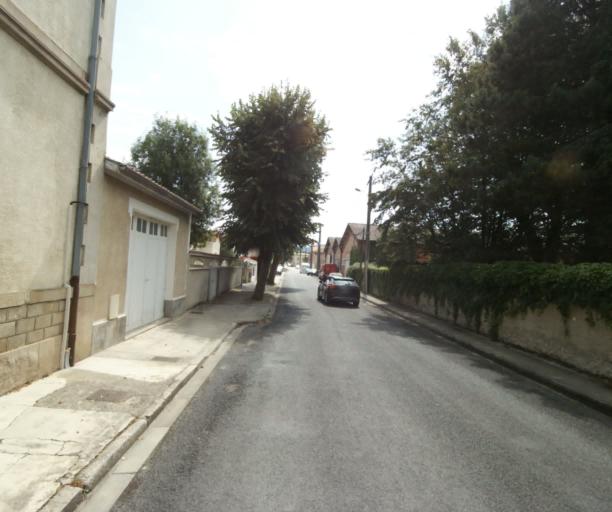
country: FR
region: Midi-Pyrenees
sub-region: Departement de la Haute-Garonne
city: Revel
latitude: 43.4625
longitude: 2.0004
